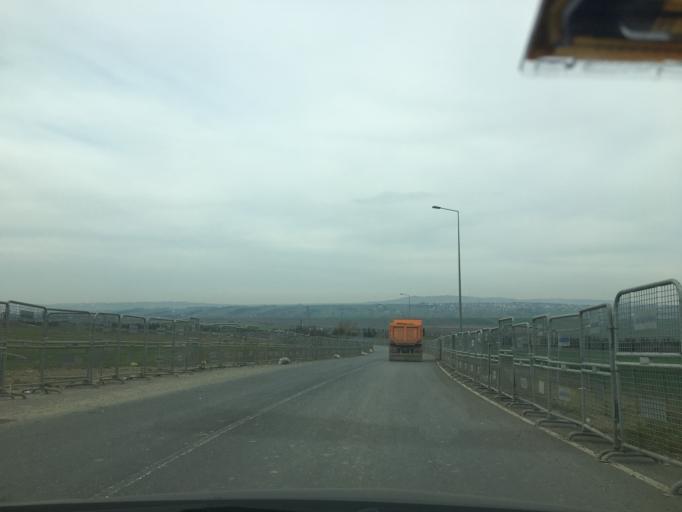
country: TR
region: Istanbul
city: Canta
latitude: 41.0961
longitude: 28.1554
